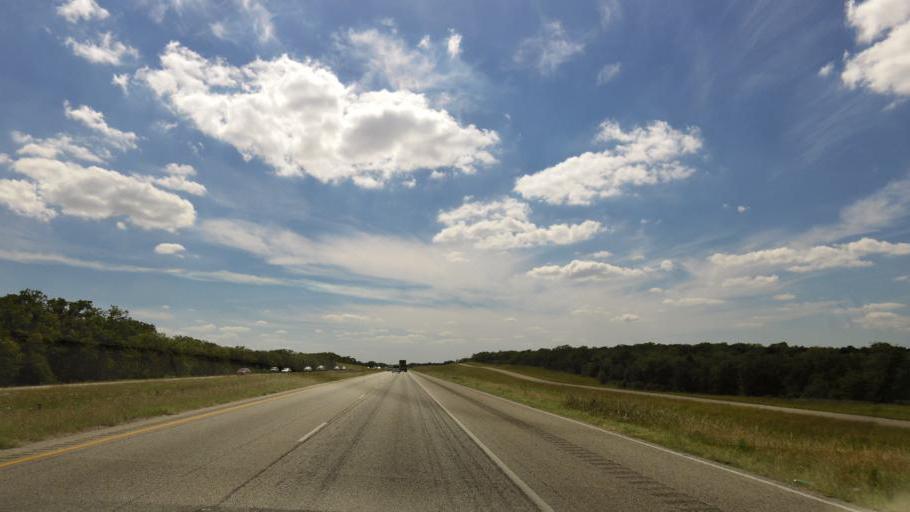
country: US
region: Texas
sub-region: Gonzales County
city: Gonzales
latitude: 29.6535
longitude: -97.4596
